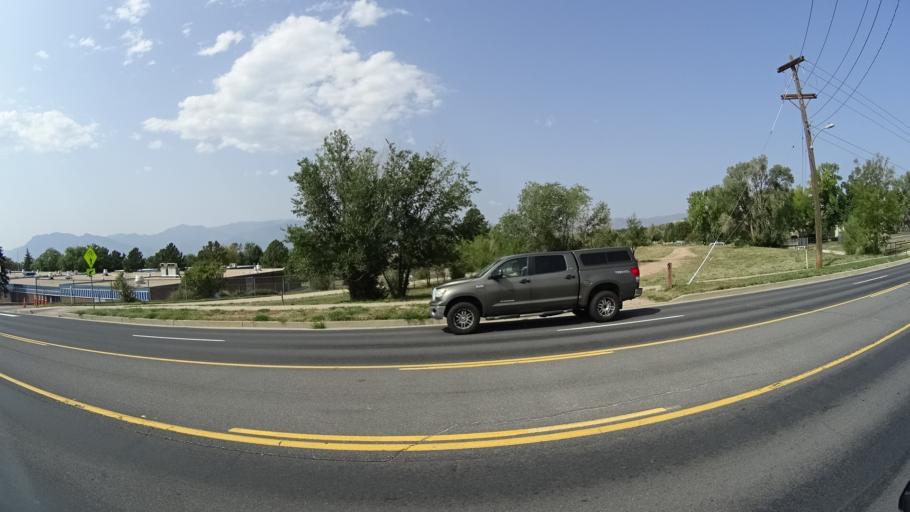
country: US
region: Colorado
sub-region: El Paso County
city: Cimarron Hills
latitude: 38.8598
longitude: -104.7479
